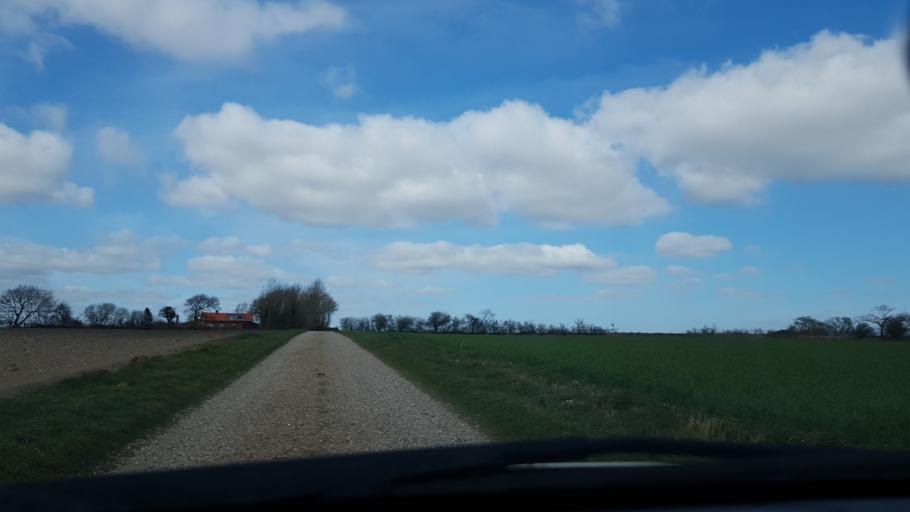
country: DK
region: South Denmark
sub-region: Haderslev Kommune
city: Gram
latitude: 55.2882
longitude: 8.9844
